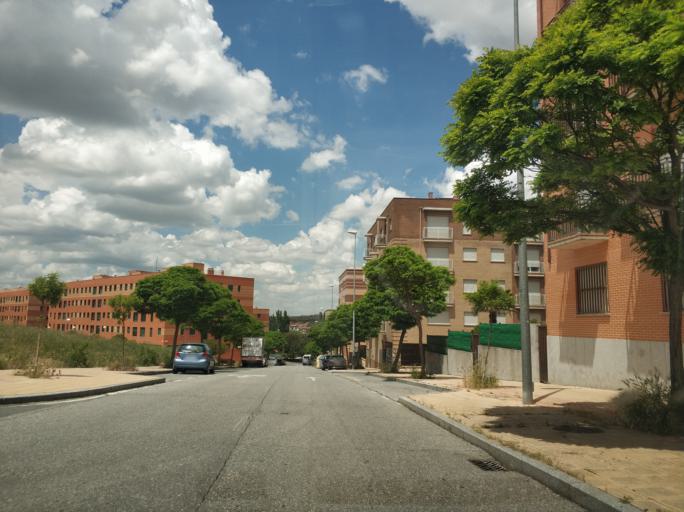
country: ES
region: Castille and Leon
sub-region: Provincia de Salamanca
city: Aldeatejada
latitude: 40.9513
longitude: -5.6885
